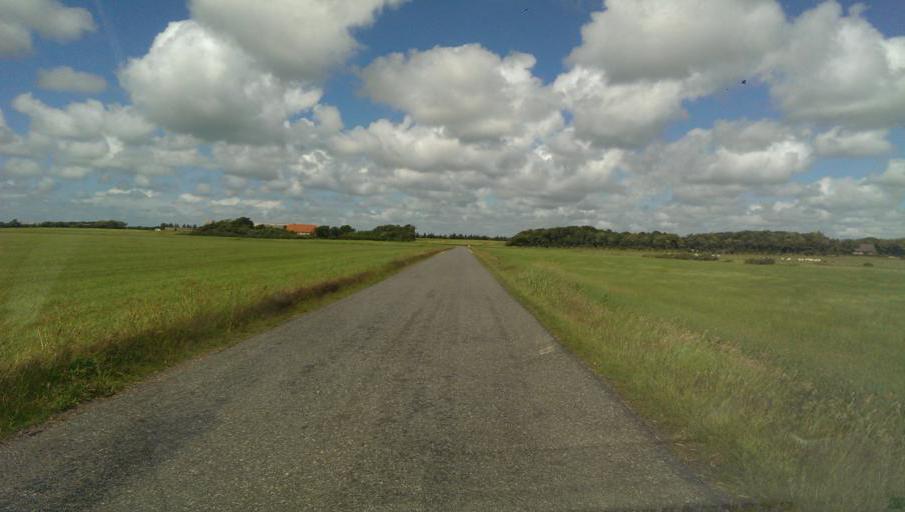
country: DK
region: Central Jutland
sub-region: Holstebro Kommune
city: Ulfborg
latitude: 56.2408
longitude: 8.2364
